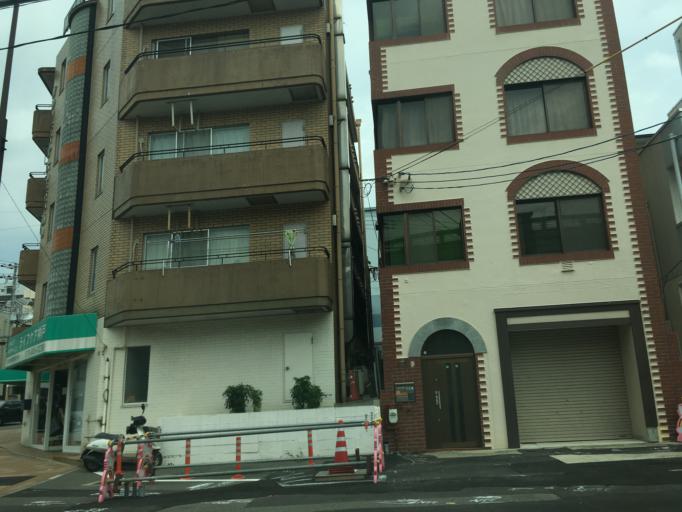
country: JP
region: Hyogo
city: Kobe
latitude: 34.7148
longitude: 135.2305
